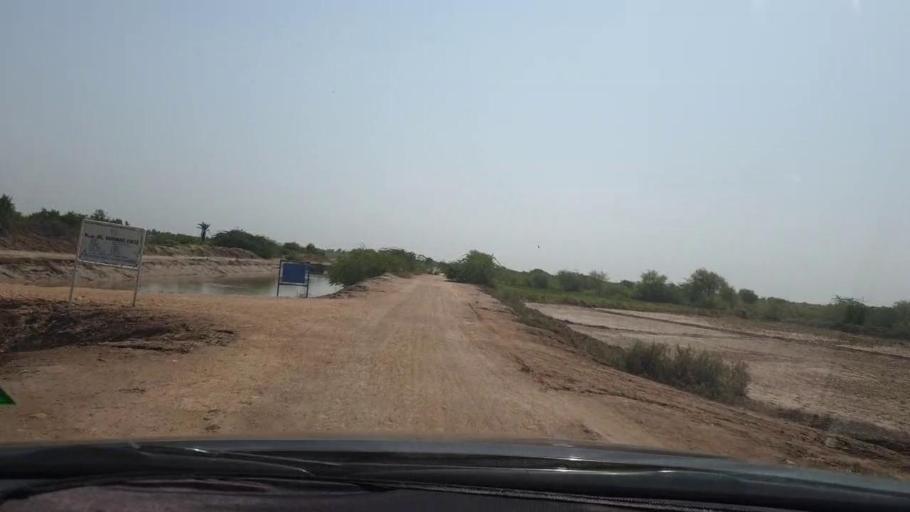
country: PK
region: Sindh
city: Tando Bago
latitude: 24.7915
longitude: 69.1141
